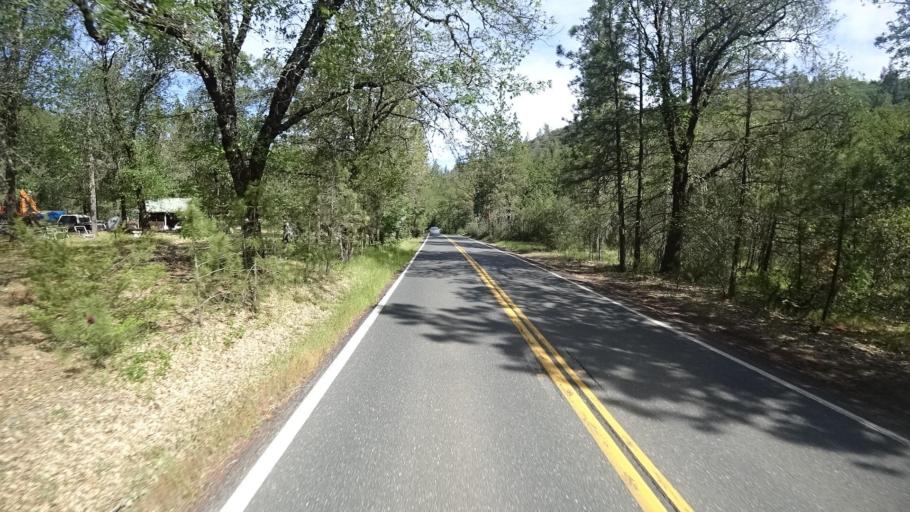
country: US
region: California
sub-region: Lake County
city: Cobb
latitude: 38.8913
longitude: -122.7342
